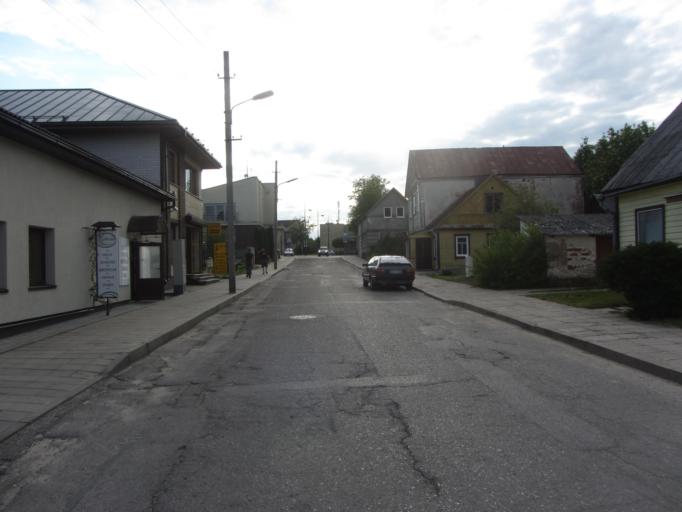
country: LT
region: Utenos apskritis
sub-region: Utena
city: Utena
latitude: 55.4946
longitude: 25.6033
